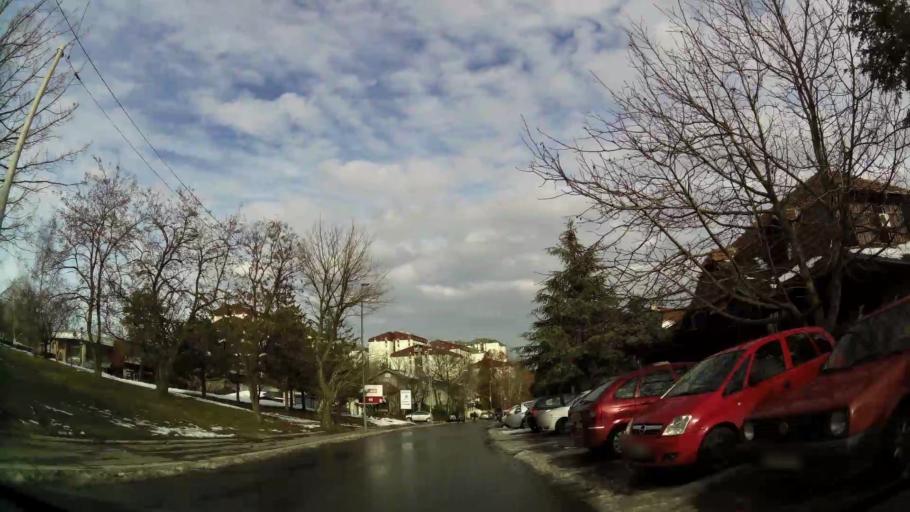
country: RS
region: Central Serbia
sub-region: Belgrade
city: Rakovica
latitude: 44.7496
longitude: 20.4352
